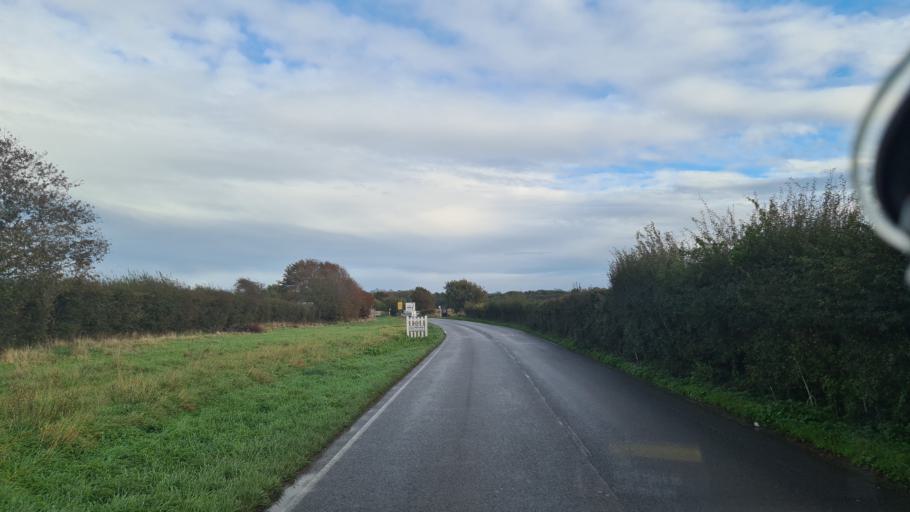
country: GB
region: England
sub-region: West Sussex
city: Walberton
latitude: 50.8120
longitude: -0.5936
